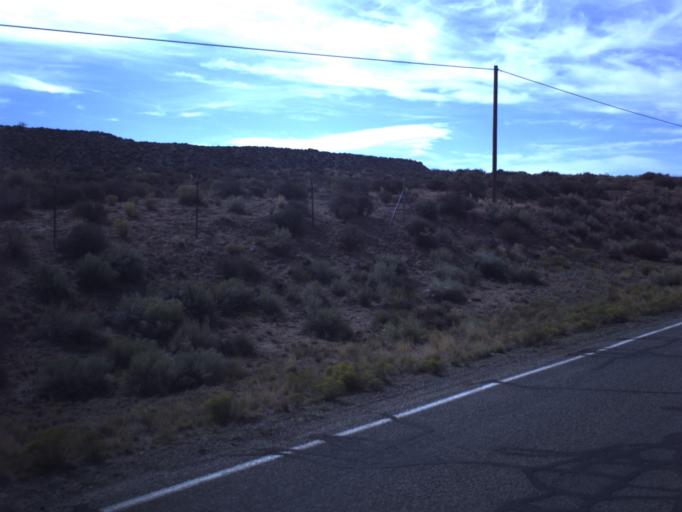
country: US
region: Utah
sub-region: San Juan County
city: Blanding
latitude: 37.2949
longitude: -109.2868
